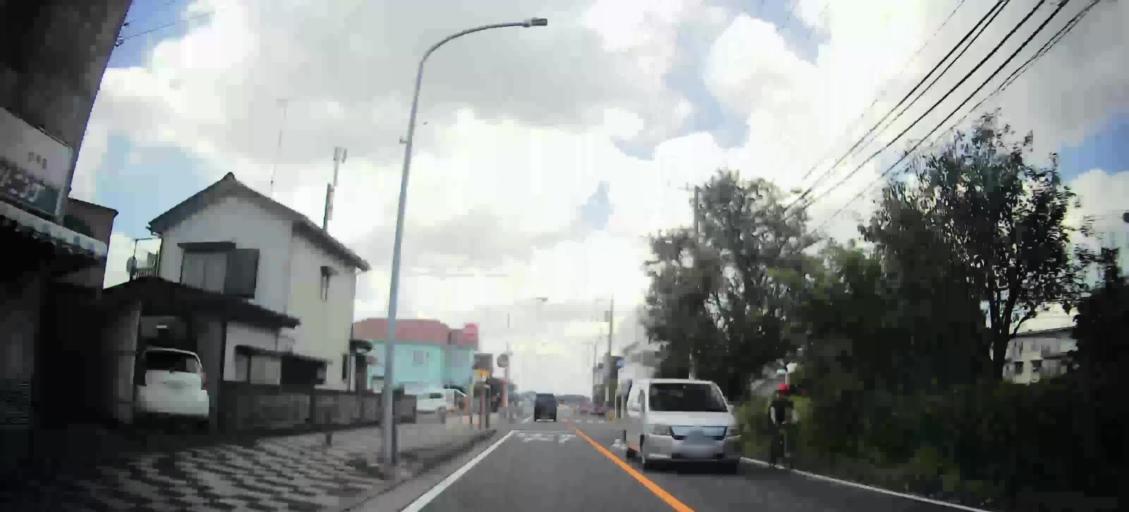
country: JP
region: Kanagawa
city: Yokohama
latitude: 35.4685
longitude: 139.5595
